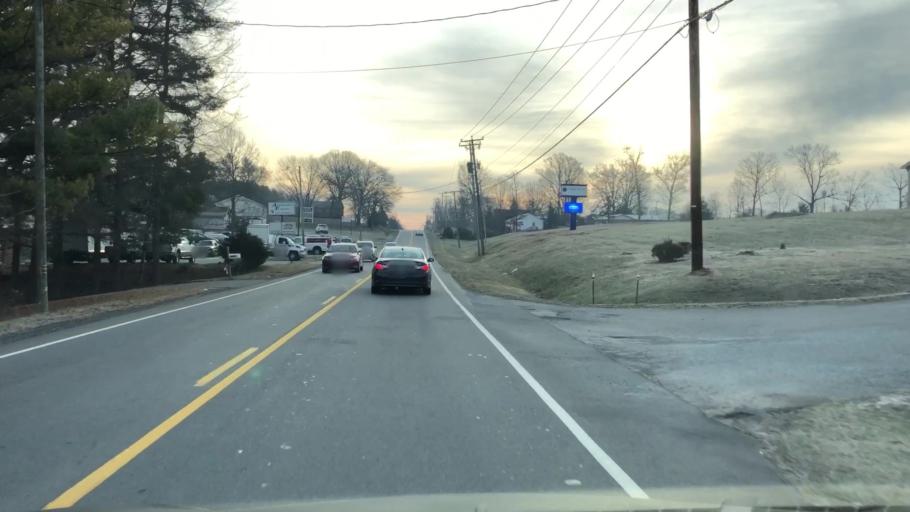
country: US
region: Virginia
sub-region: Campbell County
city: Timberlake
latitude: 37.3339
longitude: -79.2617
